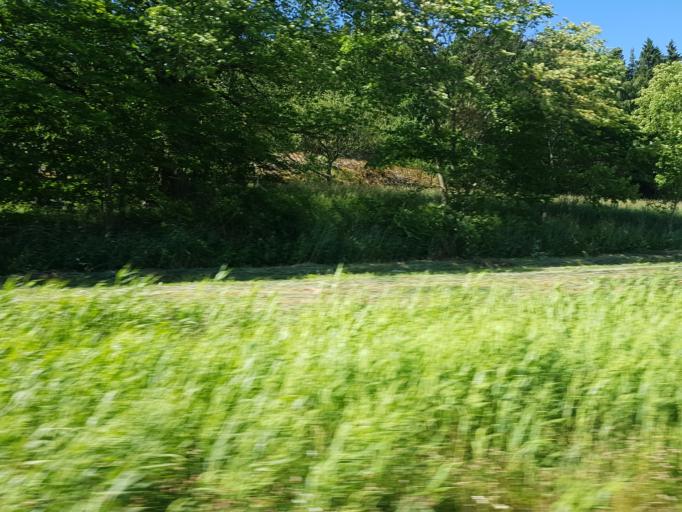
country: SE
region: Vaestra Goetaland
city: Ronnang
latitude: 57.9686
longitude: 11.6361
